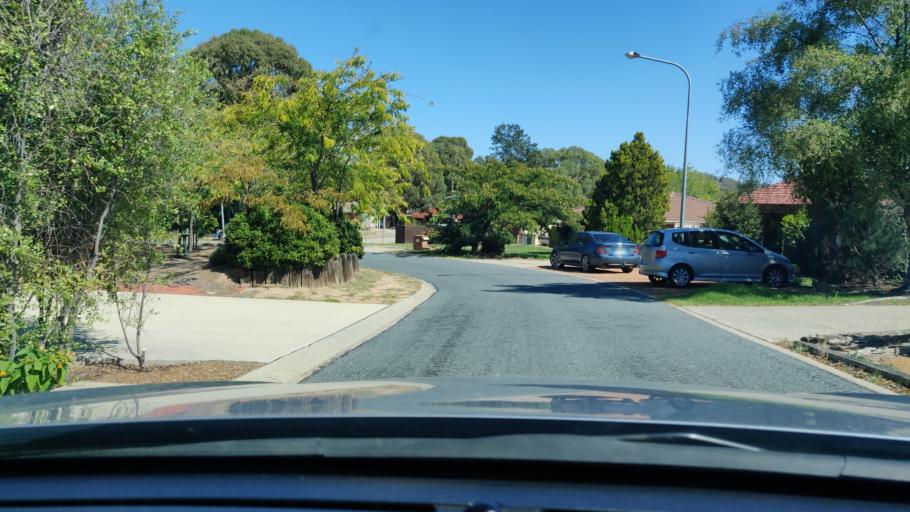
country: AU
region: Australian Capital Territory
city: Macarthur
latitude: -35.4395
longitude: 149.0952
